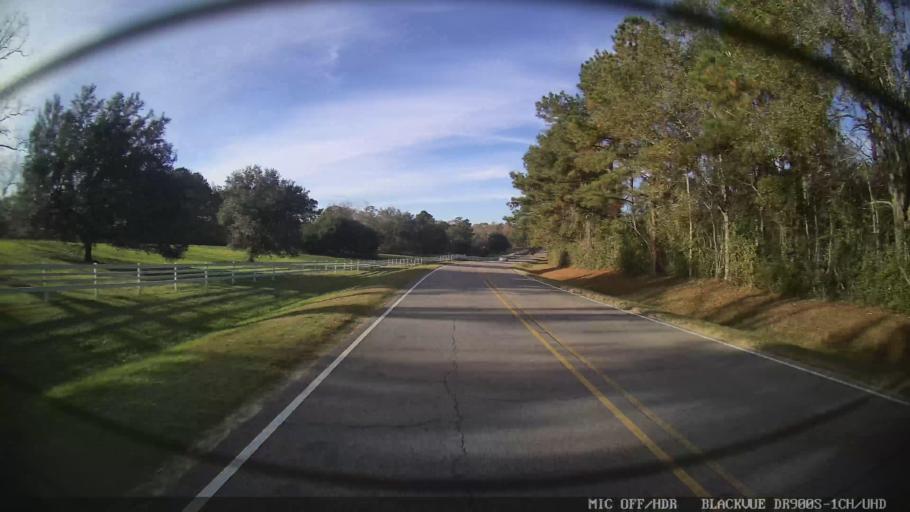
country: US
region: Mississippi
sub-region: Forrest County
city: Hattiesburg
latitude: 31.1978
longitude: -89.2912
